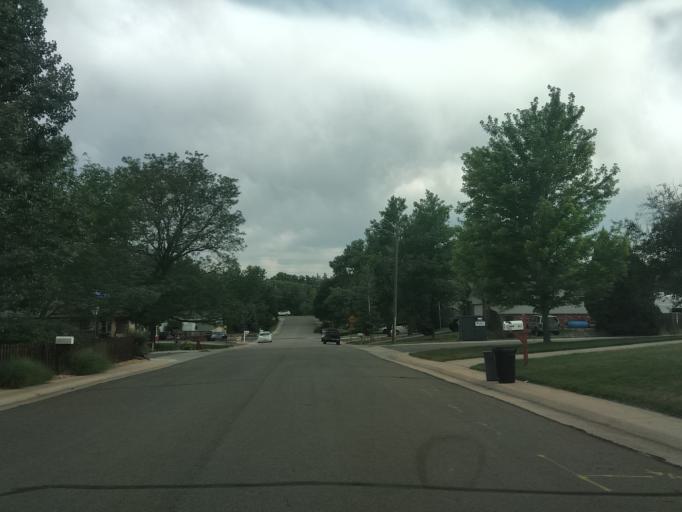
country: US
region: Colorado
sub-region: Jefferson County
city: Lakewood
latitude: 39.6988
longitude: -105.0991
